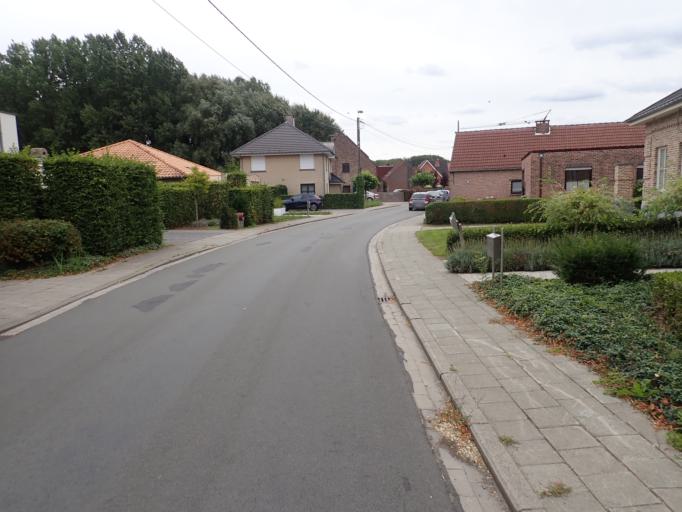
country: BE
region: Flanders
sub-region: Provincie Antwerpen
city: Puurs
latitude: 51.0487
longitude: 4.2534
